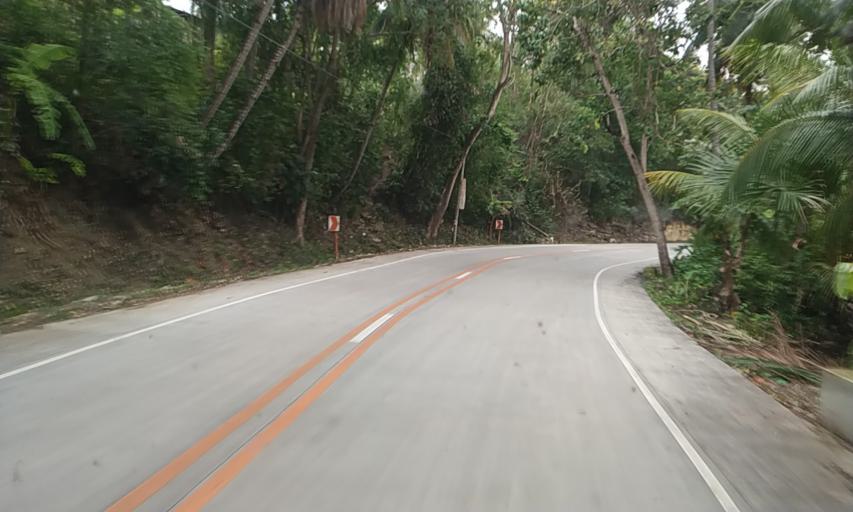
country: PH
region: Central Visayas
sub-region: Province of Negros Oriental
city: Basak
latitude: 10.2036
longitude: 123.2996
